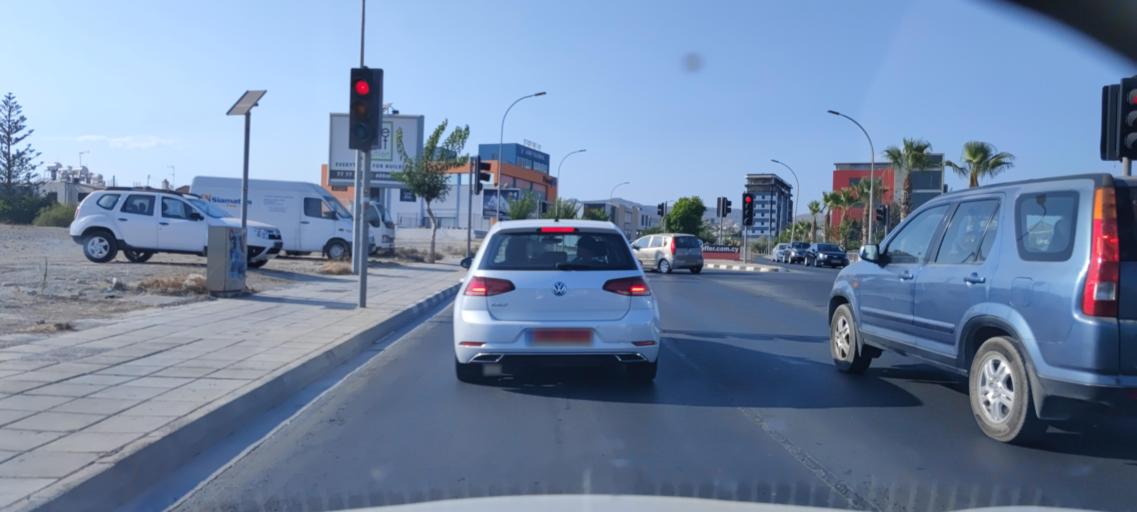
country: CY
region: Limassol
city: Limassol
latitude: 34.7013
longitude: 33.0600
